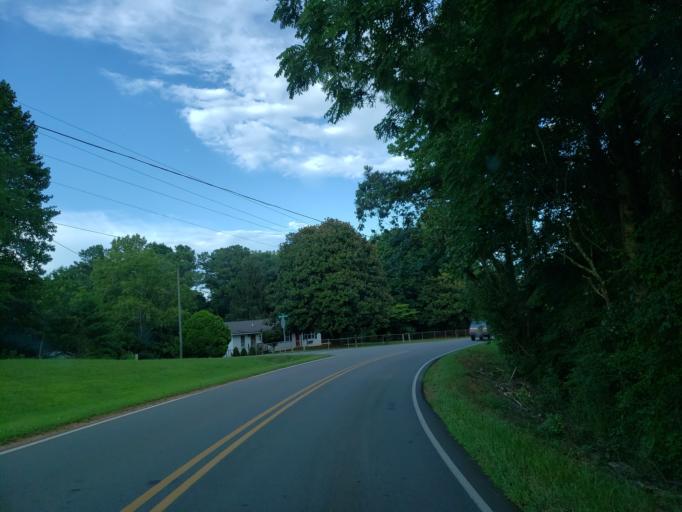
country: US
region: Georgia
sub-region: Cherokee County
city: Ball Ground
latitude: 34.3360
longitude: -84.4449
